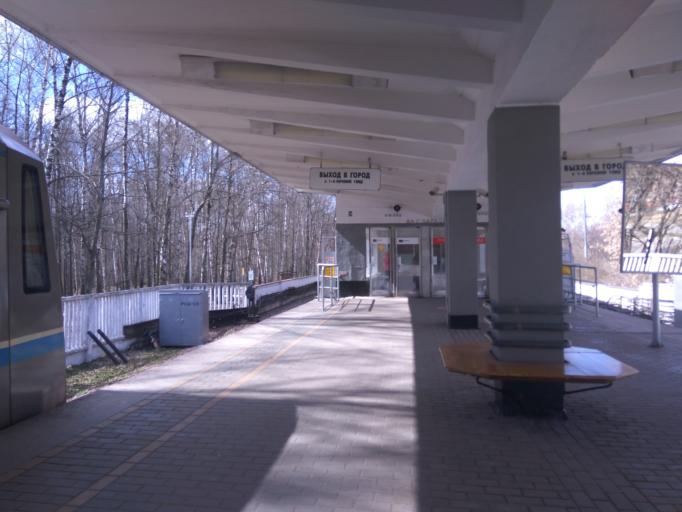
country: RU
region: Moskovskaya
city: Izmaylovo
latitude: 55.7878
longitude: 37.7808
